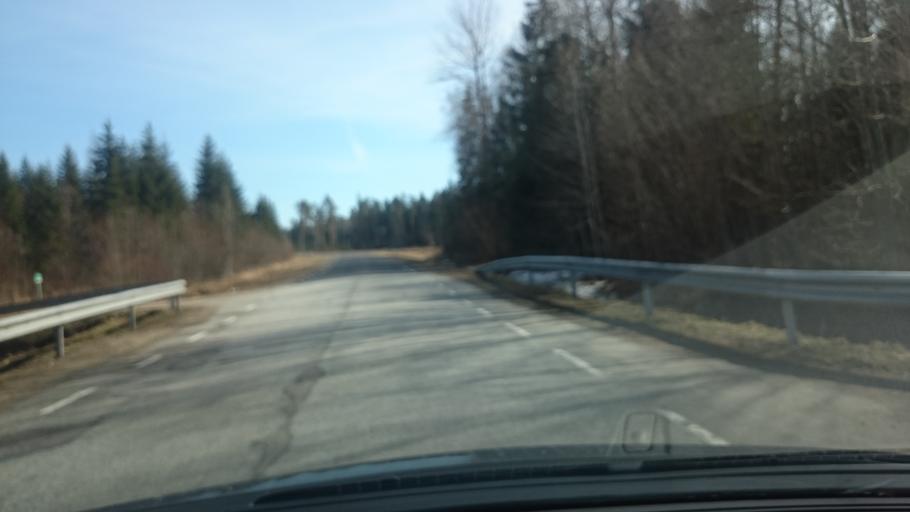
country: EE
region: Paernumaa
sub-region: Tootsi vald
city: Tootsi
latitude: 58.6421
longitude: 24.8890
